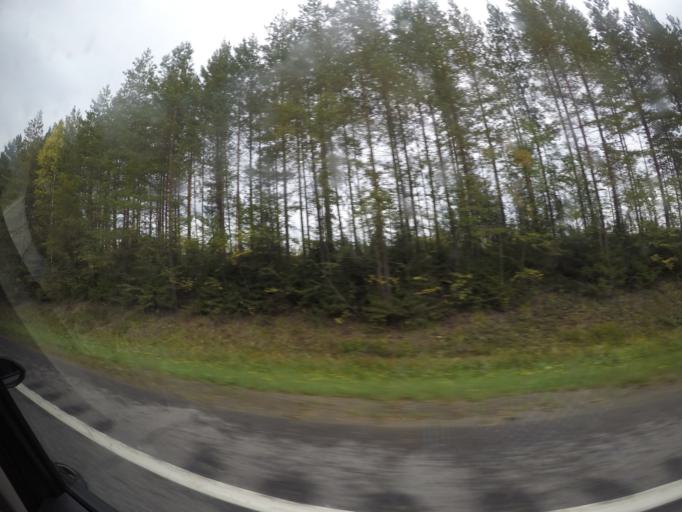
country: FI
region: Haeme
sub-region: Haemeenlinna
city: Parola
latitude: 61.1467
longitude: 24.4130
